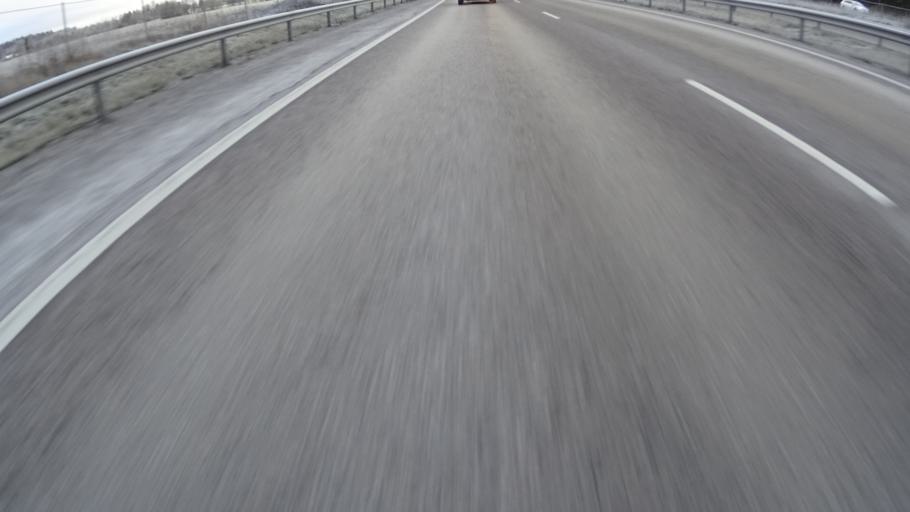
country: FI
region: Uusimaa
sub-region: Helsinki
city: Nurmijaervi
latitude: 60.3477
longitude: 24.8109
